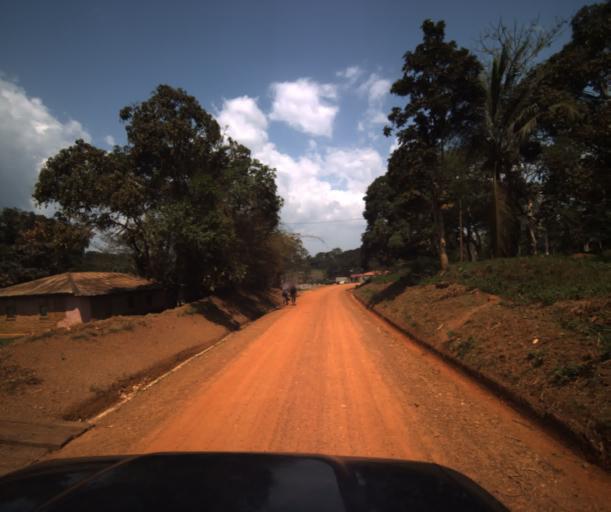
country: CM
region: Centre
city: Eseka
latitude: 3.5459
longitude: 11.0414
